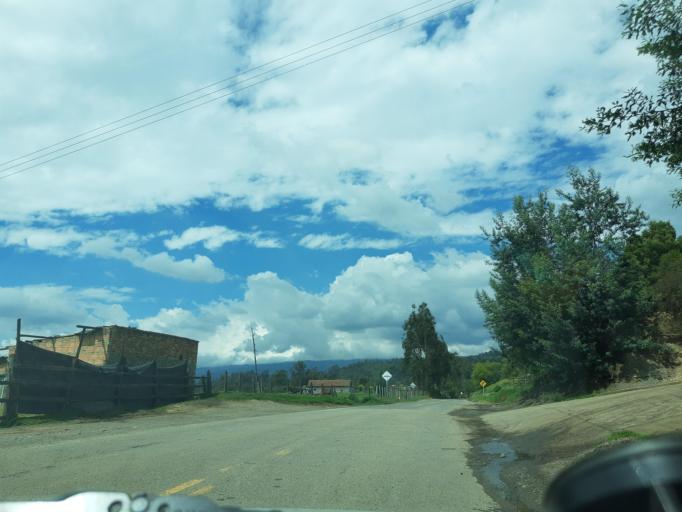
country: CO
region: Boyaca
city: Chiquinquira
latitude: 5.6154
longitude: -73.7457
